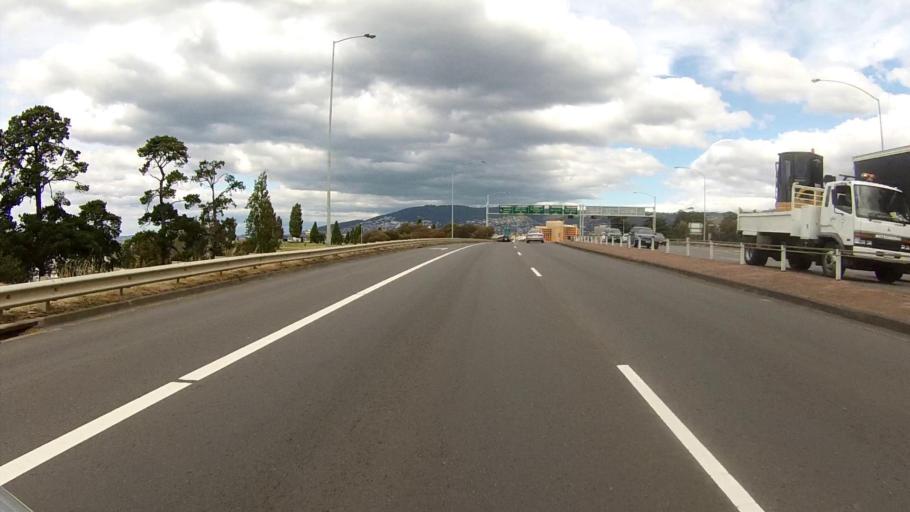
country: AU
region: Tasmania
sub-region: Hobart
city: Hobart
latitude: -42.8741
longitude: 147.3343
